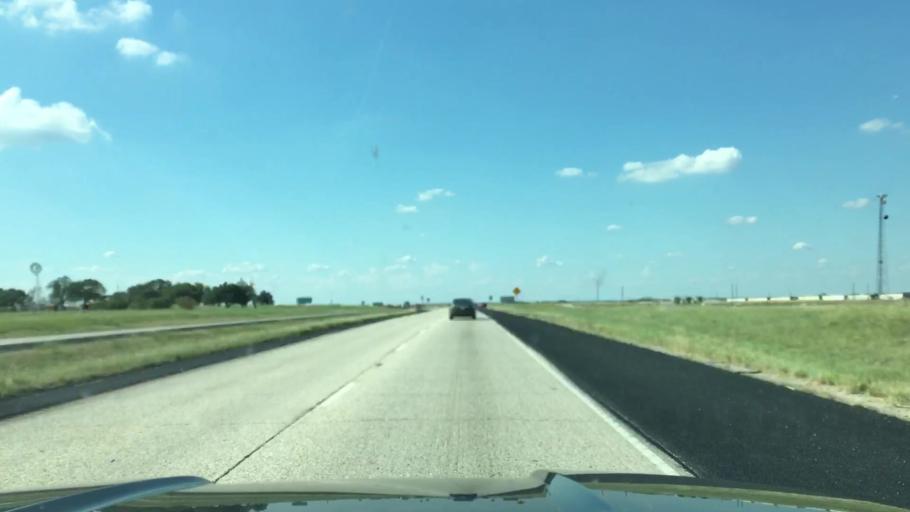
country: US
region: Texas
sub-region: Wise County
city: New Fairview
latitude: 33.1392
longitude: -97.4970
